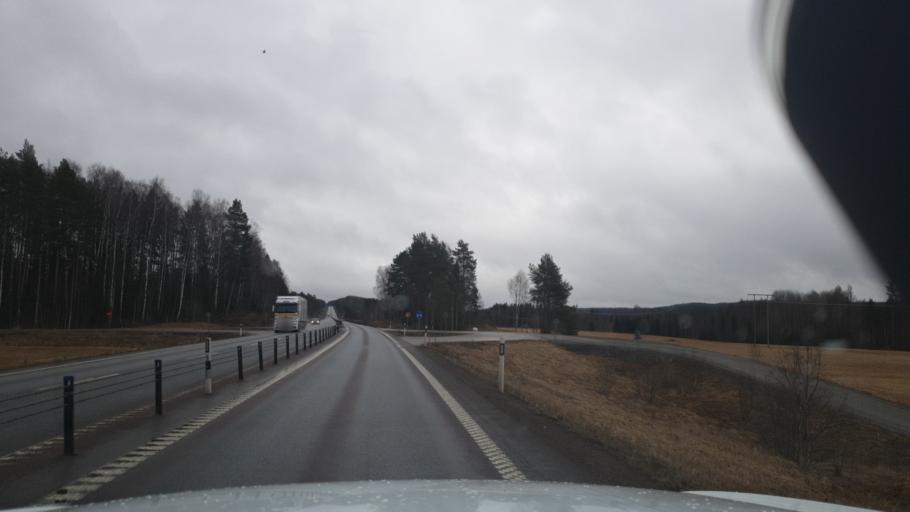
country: SE
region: Vaermland
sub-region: Arvika Kommun
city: Arvika
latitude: 59.6546
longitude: 12.6525
